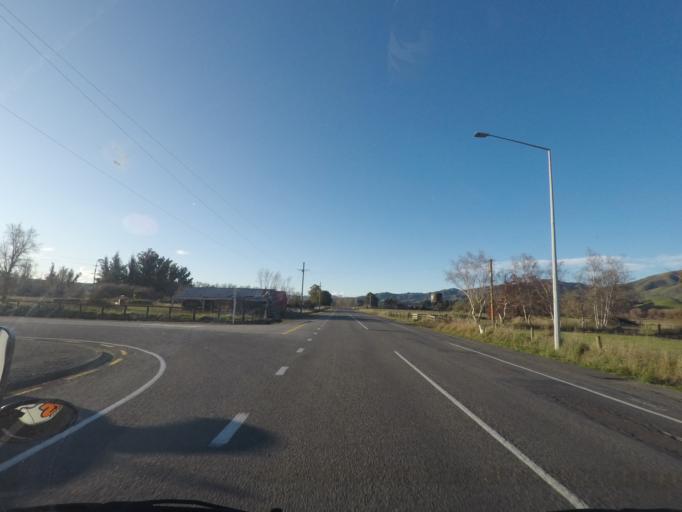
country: NZ
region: Canterbury
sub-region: Kaikoura District
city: Kaikoura
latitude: -42.7132
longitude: 173.2907
